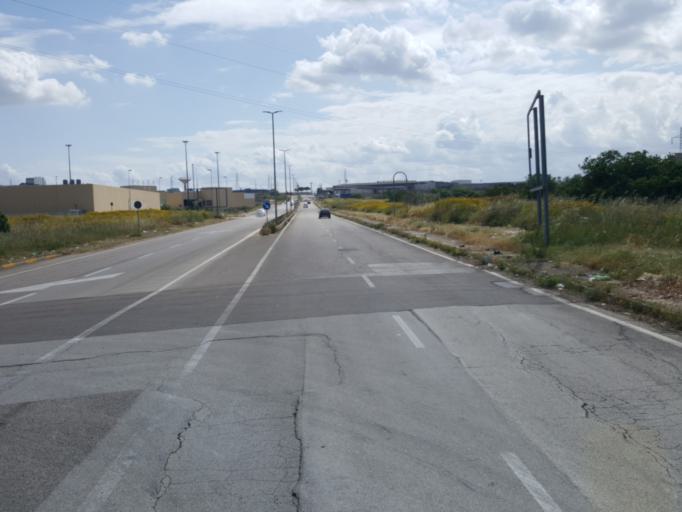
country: IT
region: Apulia
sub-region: Provincia di Bari
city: San Paolo
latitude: 41.1196
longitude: 16.8045
